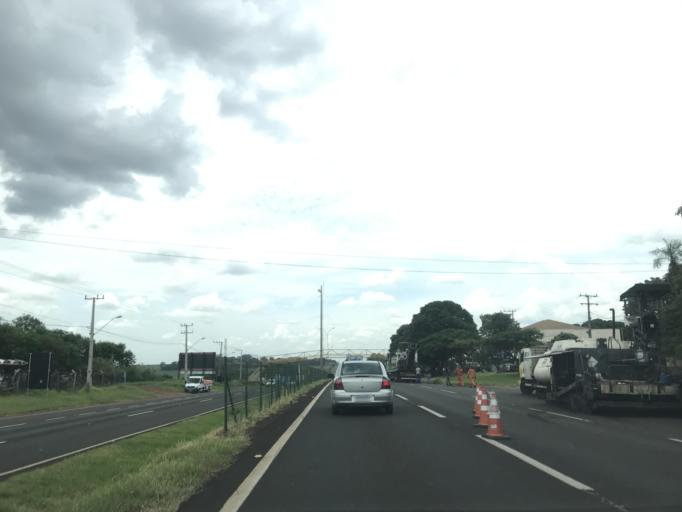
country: BR
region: Parana
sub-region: Mandaguacu
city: Mandaguacu
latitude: -23.3832
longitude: -52.0312
